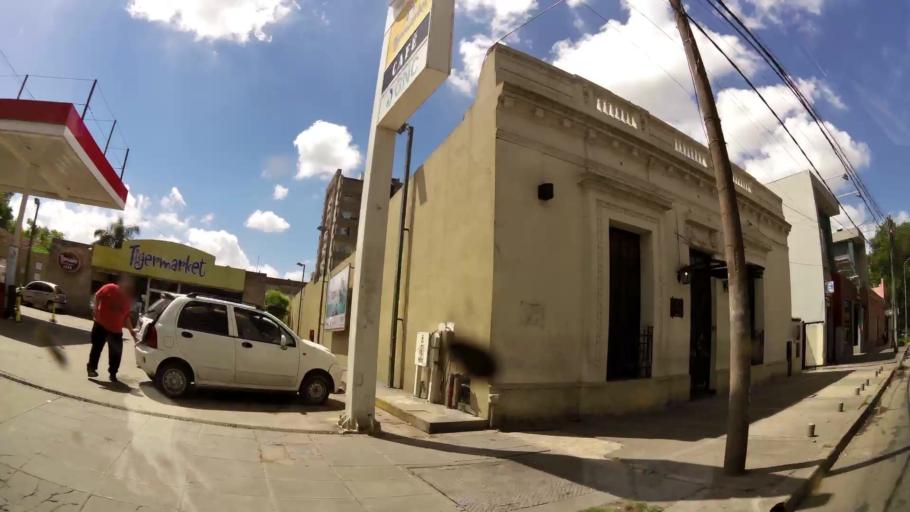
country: AR
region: Buenos Aires
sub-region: Partido de Quilmes
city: Quilmes
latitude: -34.8090
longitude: -58.2775
